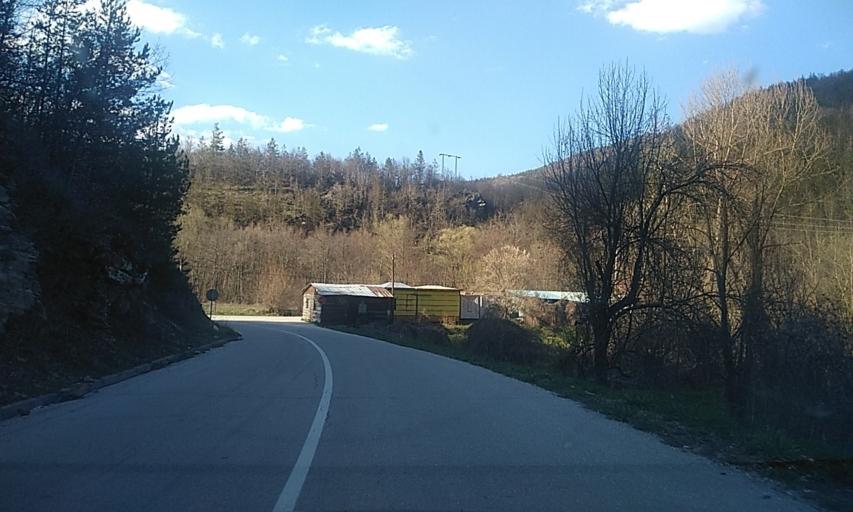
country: RS
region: Central Serbia
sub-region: Pcinjski Okrug
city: Bosilegrad
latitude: 42.4177
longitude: 22.5243
